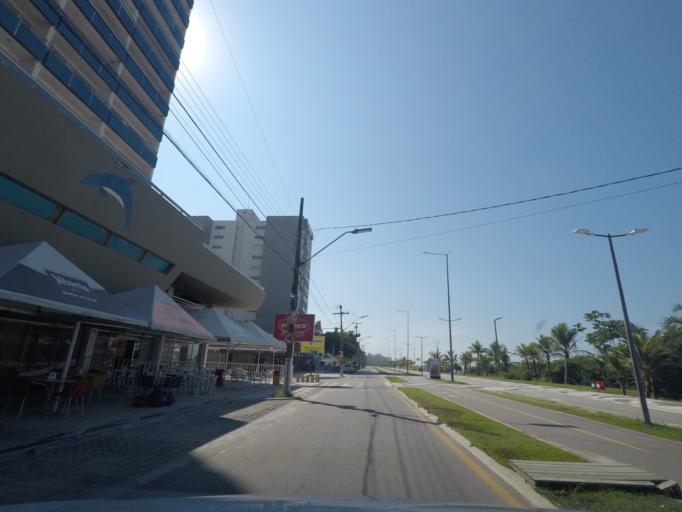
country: BR
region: Parana
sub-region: Guaratuba
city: Guaratuba
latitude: -25.8374
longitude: -48.5381
